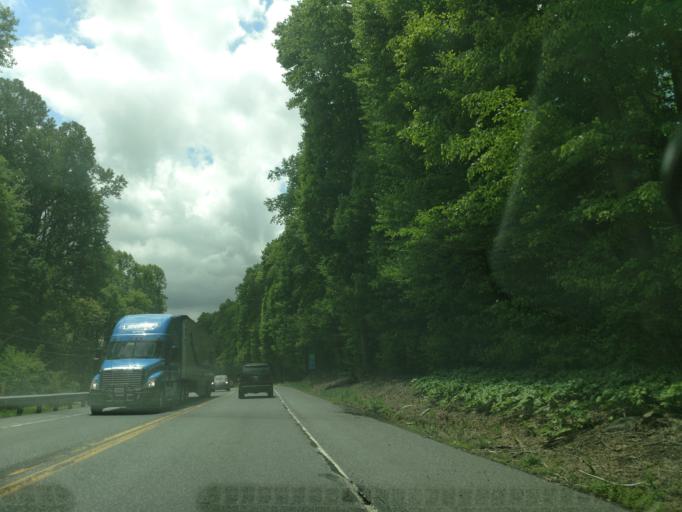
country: US
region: Pennsylvania
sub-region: Lebanon County
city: Cornwall
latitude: 40.2519
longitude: -76.4340
